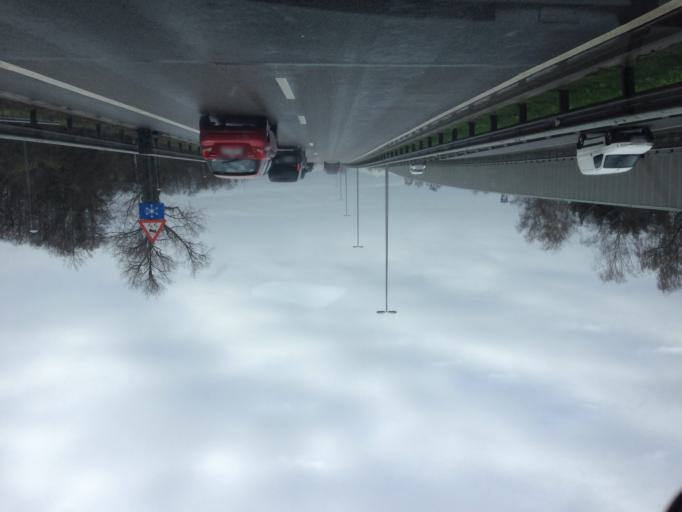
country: BE
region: Flanders
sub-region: Provincie Limburg
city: Genk
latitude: 50.9742
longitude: 5.4908
